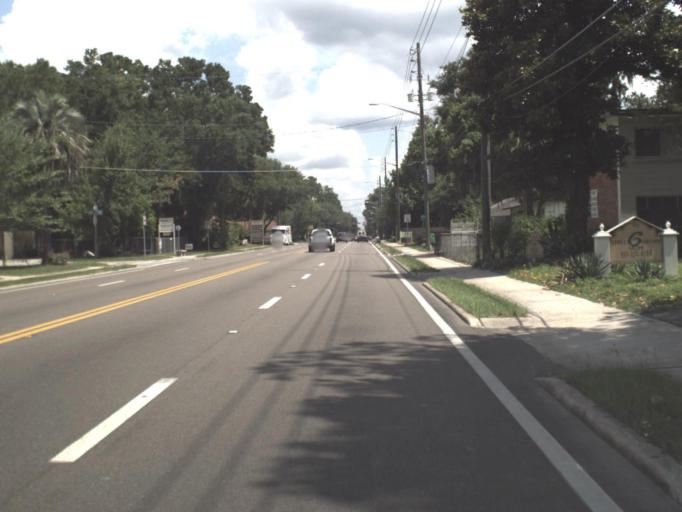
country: US
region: Florida
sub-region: Alachua County
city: Gainesville
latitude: 29.6632
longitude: -82.3308
